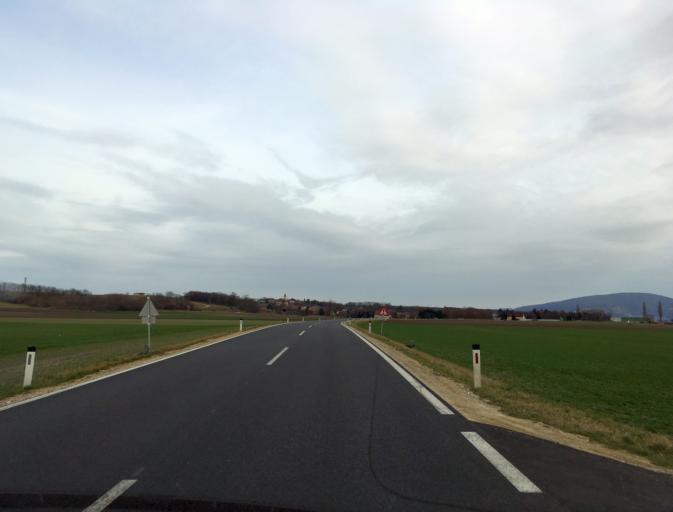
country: AT
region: Lower Austria
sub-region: Politischer Bezirk Ganserndorf
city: Engelhartstetten
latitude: 48.2214
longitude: 16.8900
